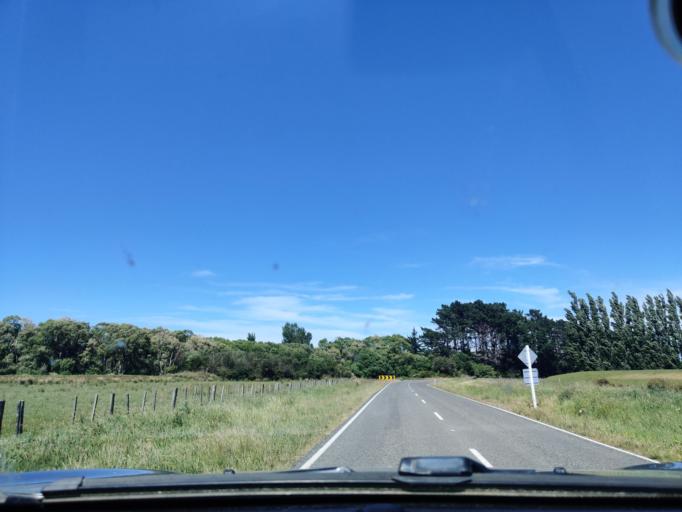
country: NZ
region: Wellington
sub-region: Upper Hutt City
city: Upper Hutt
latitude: -41.3681
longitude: 175.1858
